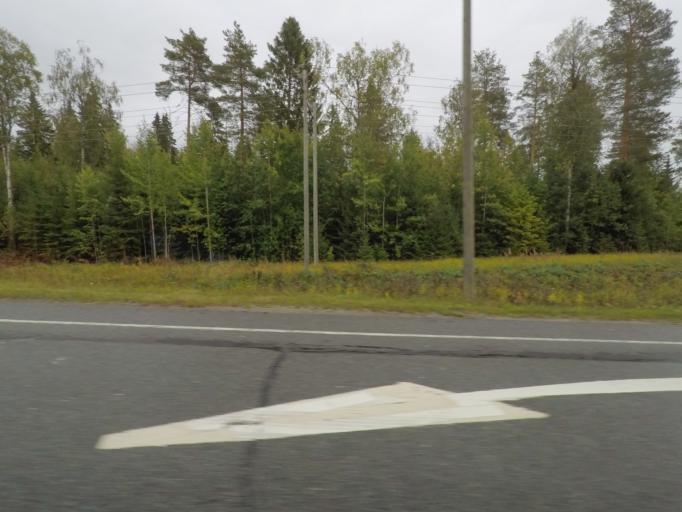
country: FI
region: Southern Savonia
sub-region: Pieksaemaeki
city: Juva
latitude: 61.9028
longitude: 27.8042
